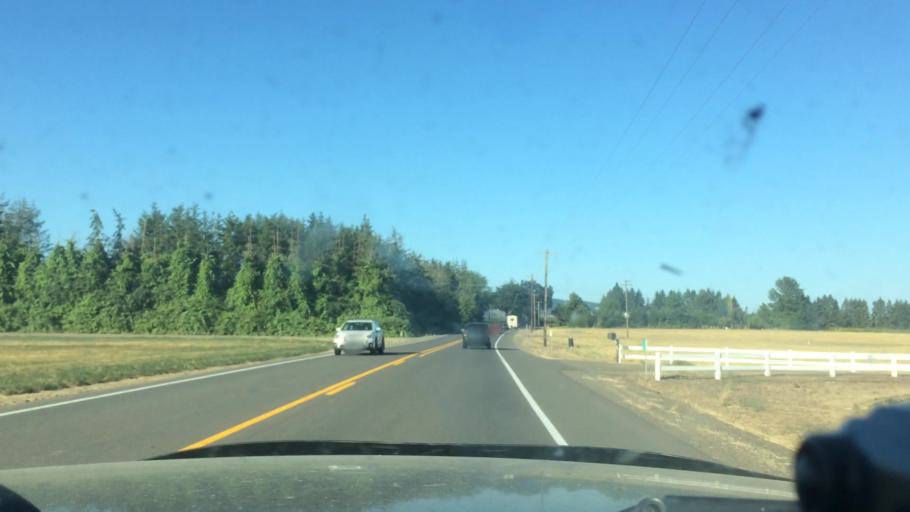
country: US
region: Oregon
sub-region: Yamhill County
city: Newberg
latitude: 45.2409
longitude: -122.9535
